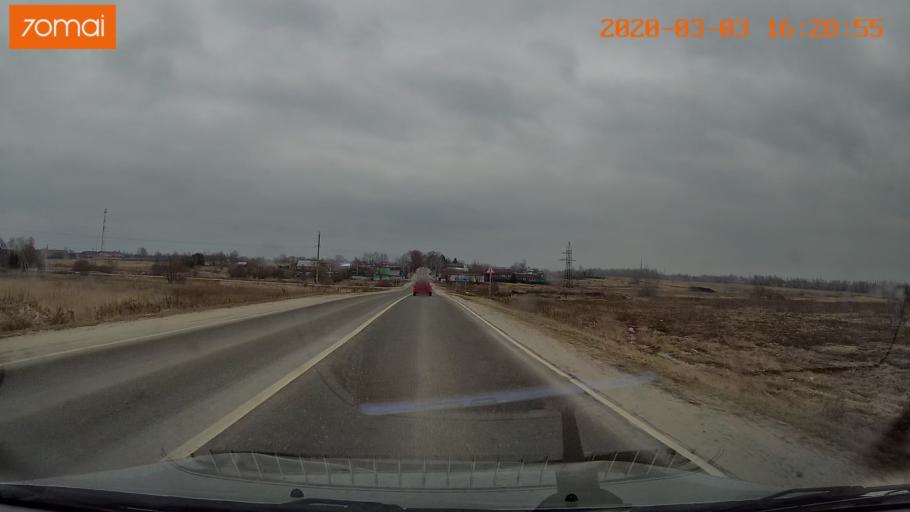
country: RU
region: Moskovskaya
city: Konobeyevo
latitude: 55.4383
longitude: 38.6949
